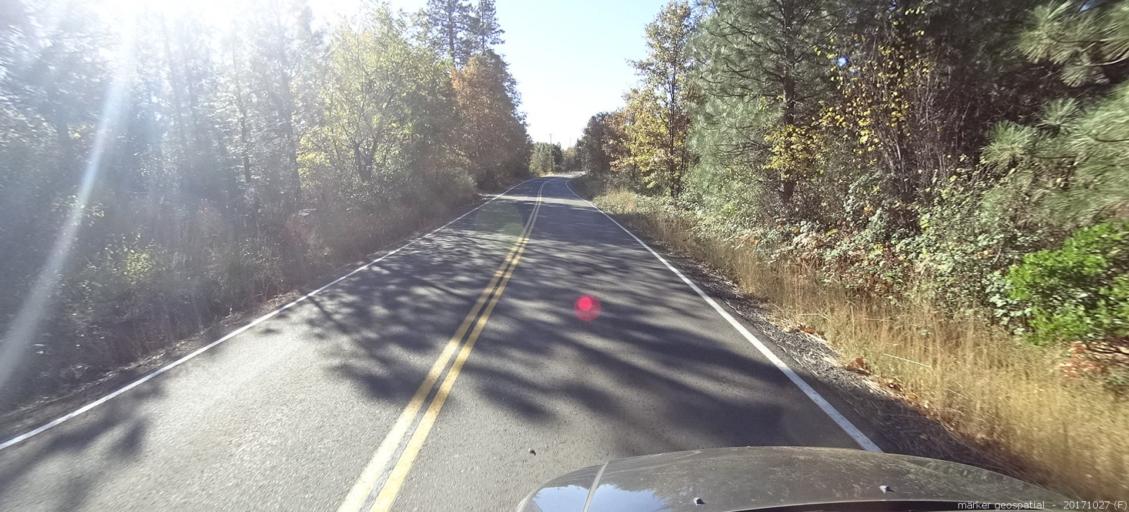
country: US
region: California
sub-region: Shasta County
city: Burney
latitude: 40.8828
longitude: -121.9083
